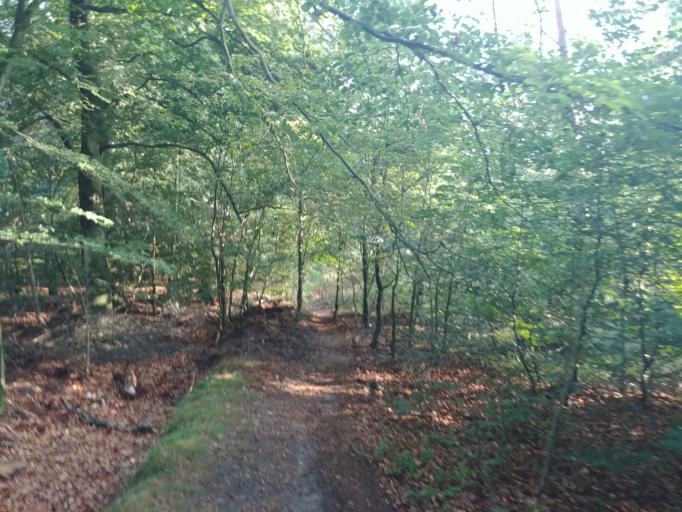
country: NL
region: Gelderland
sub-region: Gemeente Renkum
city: Wolfheze
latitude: 52.0365
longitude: 5.7720
